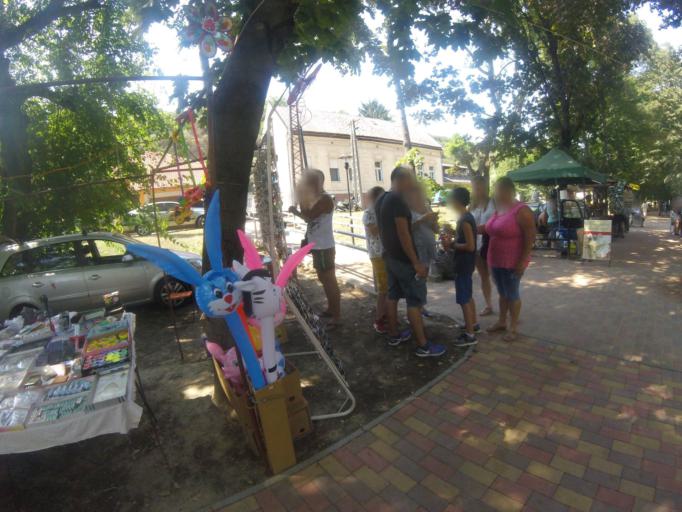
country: HU
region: Tolna
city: Dunafoldvar
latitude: 46.8104
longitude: 18.9279
